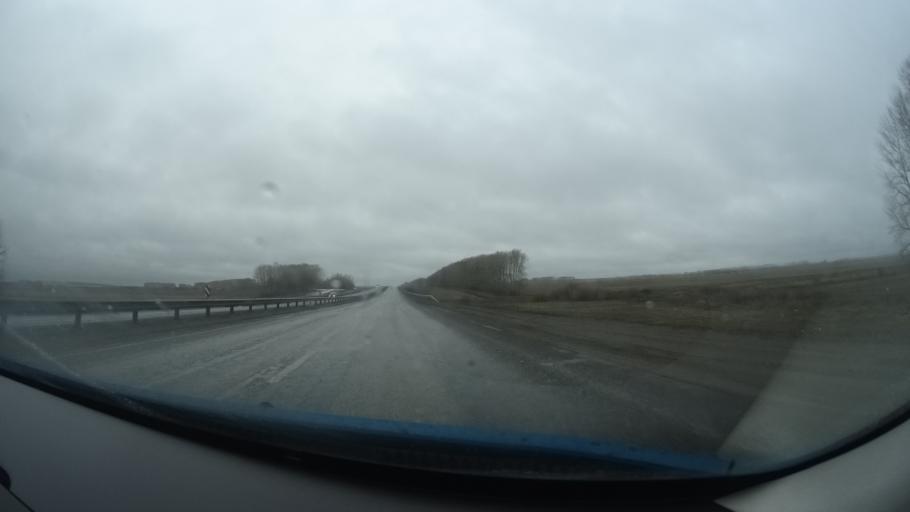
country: RU
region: Bashkortostan
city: Dmitriyevka
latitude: 54.7152
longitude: 55.1999
